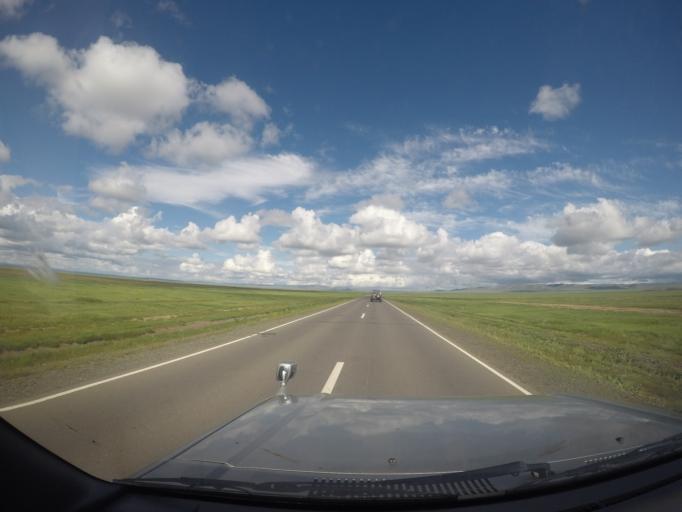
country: MN
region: Hentiy
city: Moron
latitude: 47.4196
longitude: 109.9935
